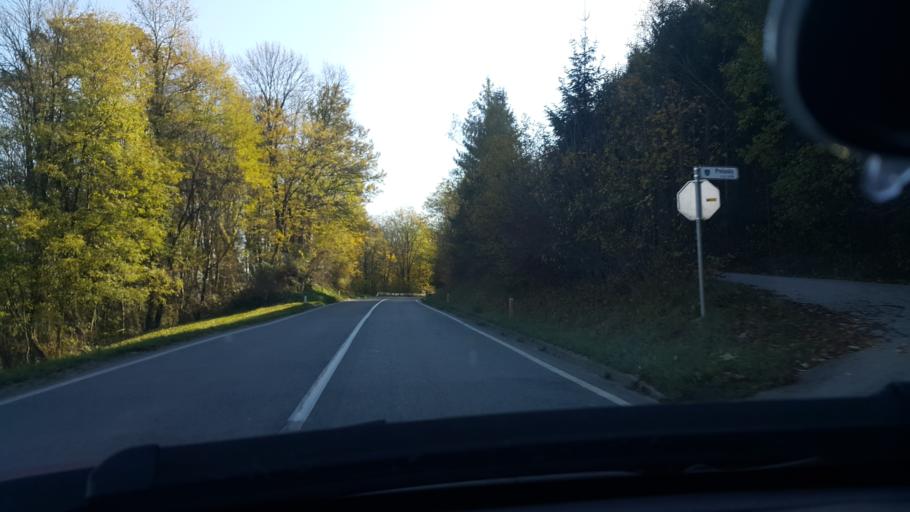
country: SI
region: Podcetrtek
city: Podcetrtek
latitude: 46.1145
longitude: 15.5999
